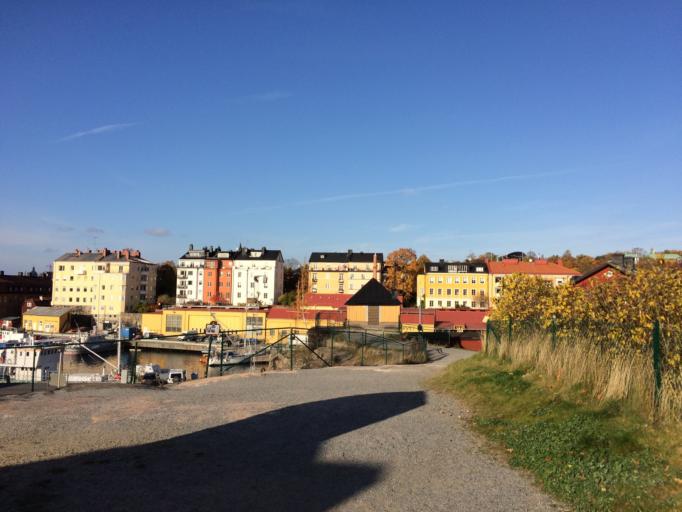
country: SE
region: Stockholm
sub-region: Stockholms Kommun
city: OEstermalm
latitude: 59.3211
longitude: 18.1006
